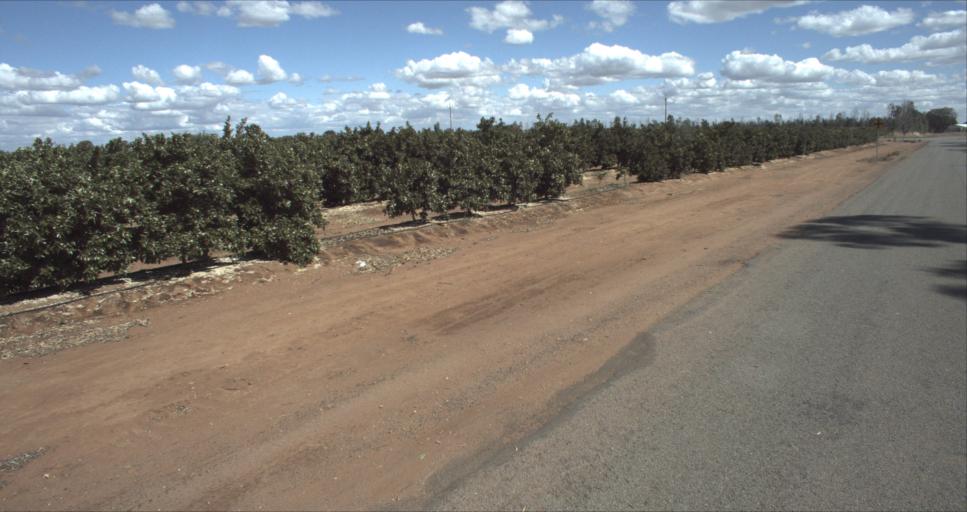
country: AU
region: New South Wales
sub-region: Leeton
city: Leeton
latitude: -34.5168
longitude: 146.2363
